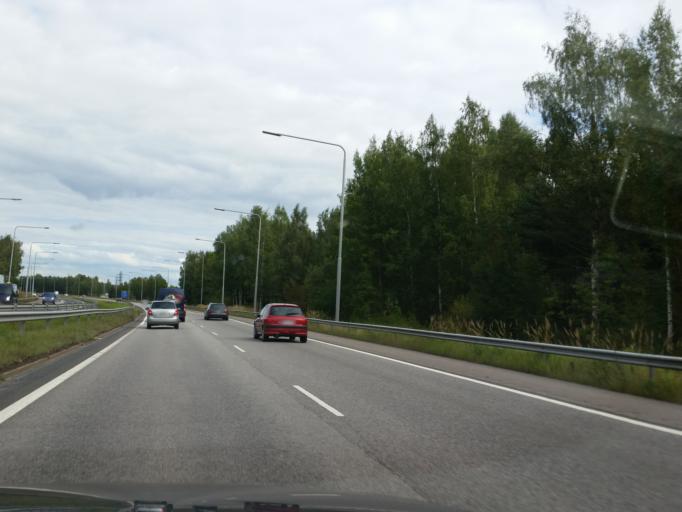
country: FI
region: Uusimaa
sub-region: Helsinki
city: Helsinki
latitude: 60.2575
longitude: 24.9570
